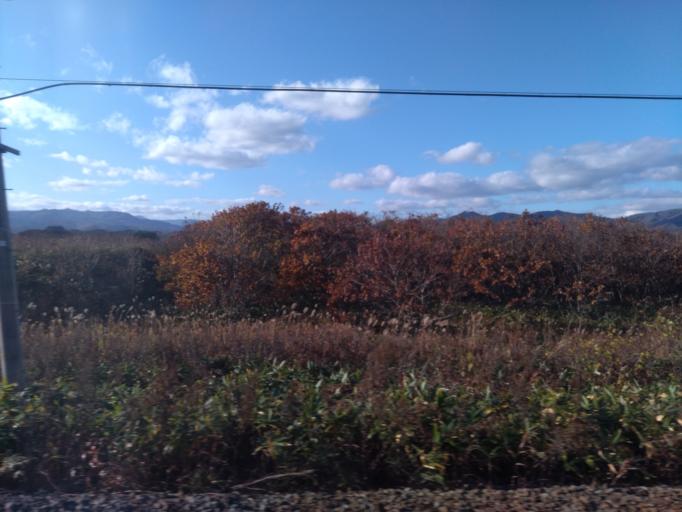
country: JP
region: Hokkaido
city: Niseko Town
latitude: 42.5346
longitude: 140.3996
